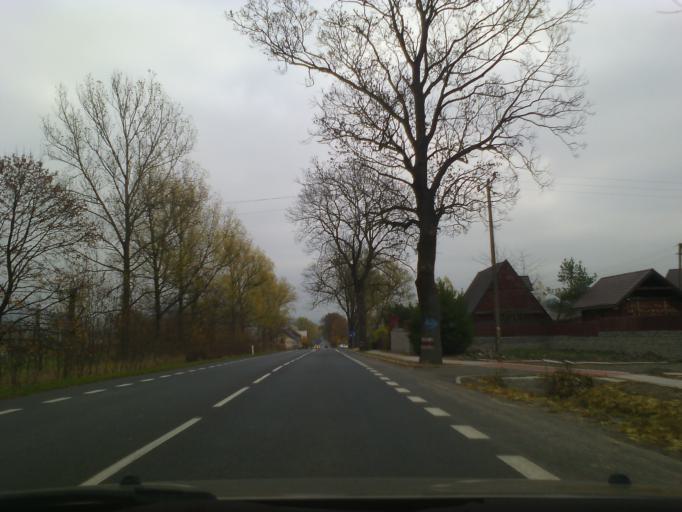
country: PL
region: Lower Silesian Voivodeship
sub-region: Powiat walbrzyski
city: Czarny Bor
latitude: 50.7804
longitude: 16.1044
